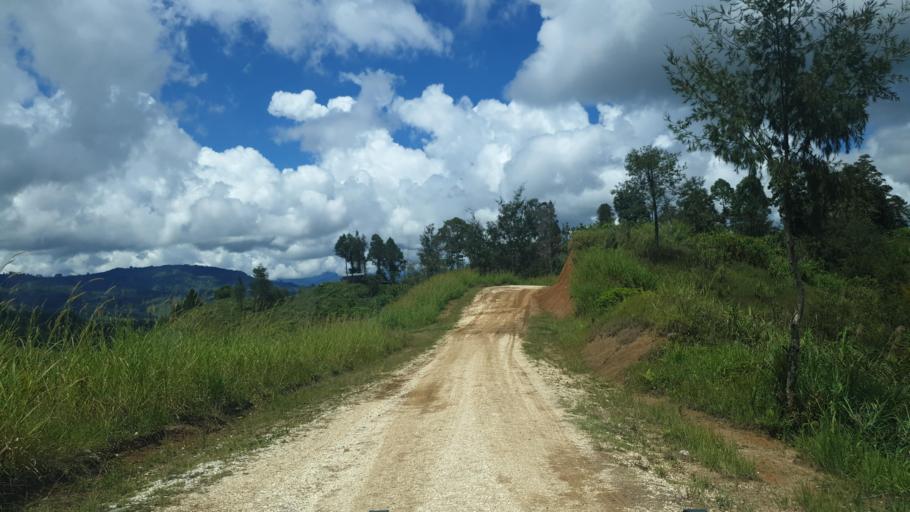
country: PG
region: Chimbu
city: Kundiawa
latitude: -6.2168
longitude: 145.1369
